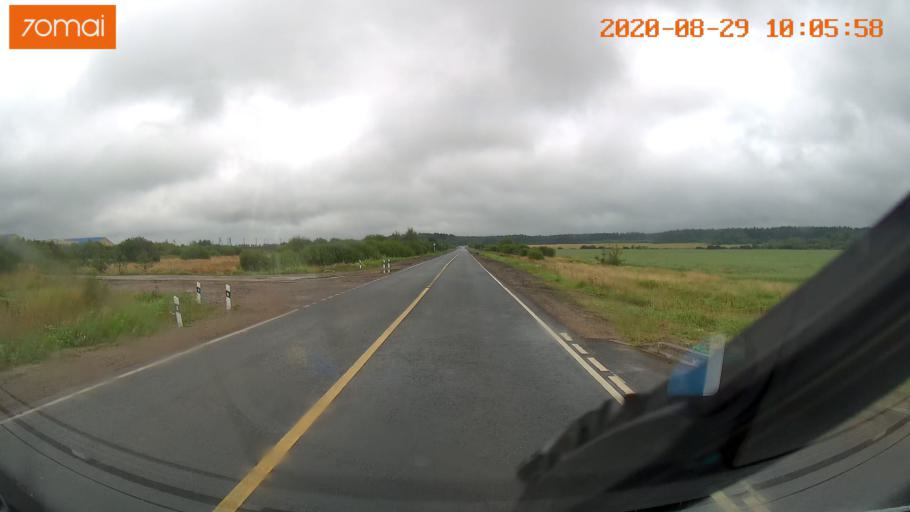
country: RU
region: Ivanovo
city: Zarechnyy
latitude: 57.3907
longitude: 42.5344
